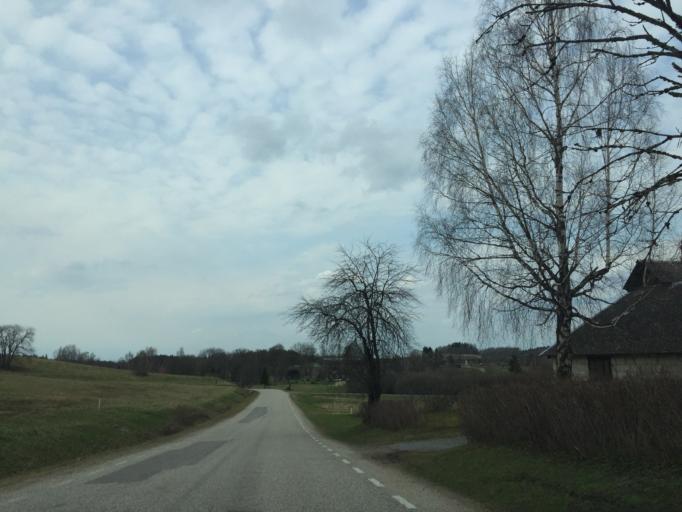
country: EE
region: Vorumaa
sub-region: Voru linn
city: Voru
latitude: 57.7154
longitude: 27.0550
